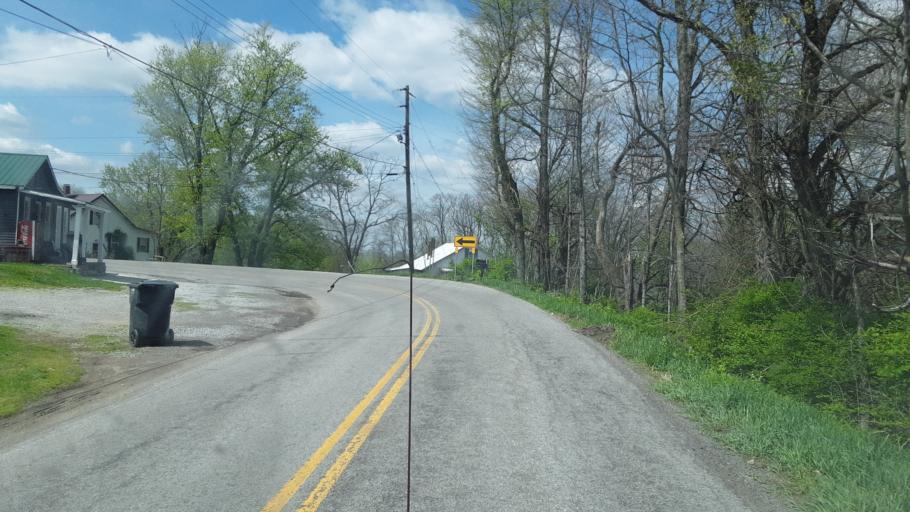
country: US
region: Kentucky
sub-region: Owen County
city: Owenton
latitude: 38.6400
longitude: -84.7749
